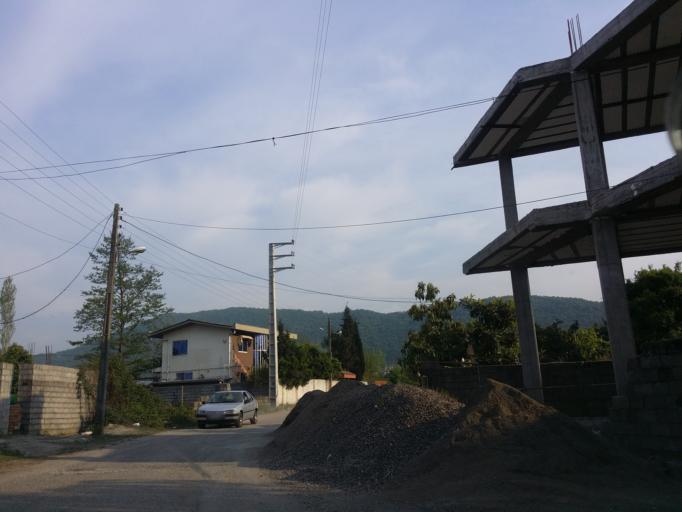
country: IR
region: Mazandaran
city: Chalus
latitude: 36.6584
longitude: 51.3674
